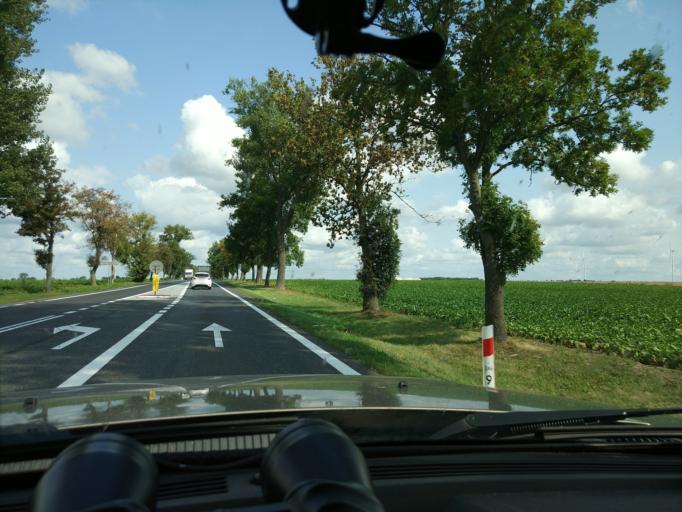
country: PL
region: Masovian Voivodeship
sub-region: Powiat mlawski
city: Wisniewo
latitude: 53.0367
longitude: 20.3396
